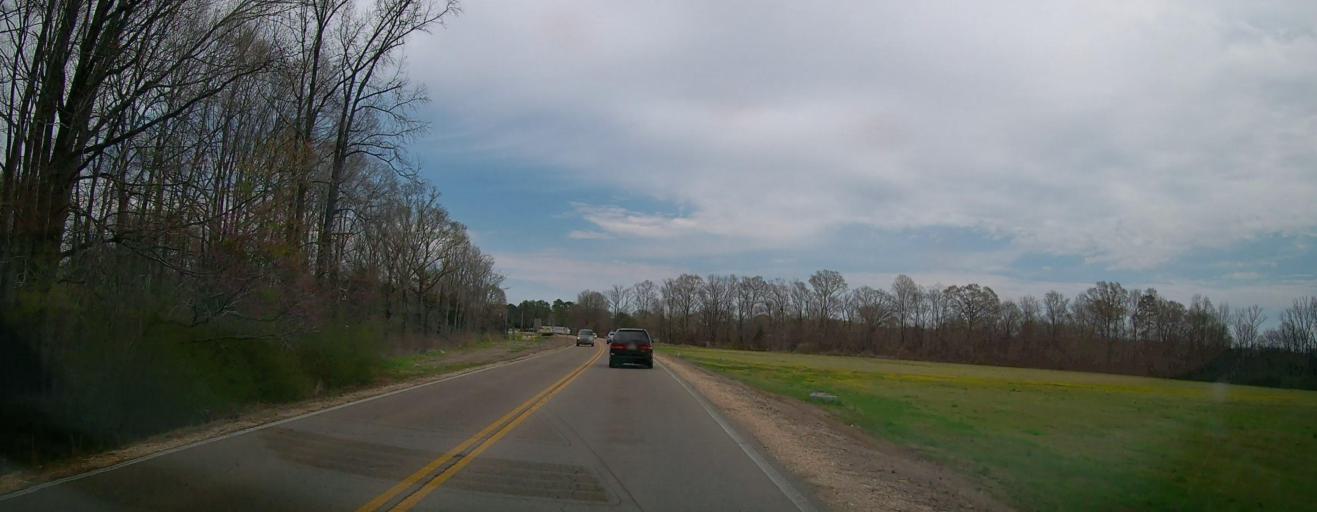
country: US
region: Mississippi
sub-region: Lee County
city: Plantersville
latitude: 34.2586
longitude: -88.6525
